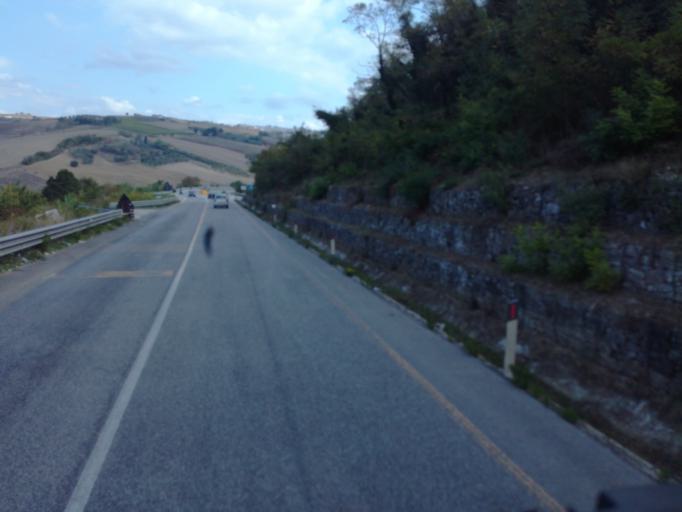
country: IT
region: Campania
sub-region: Provincia di Benevento
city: Fragneto Monforte
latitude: 41.2216
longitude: 14.7417
